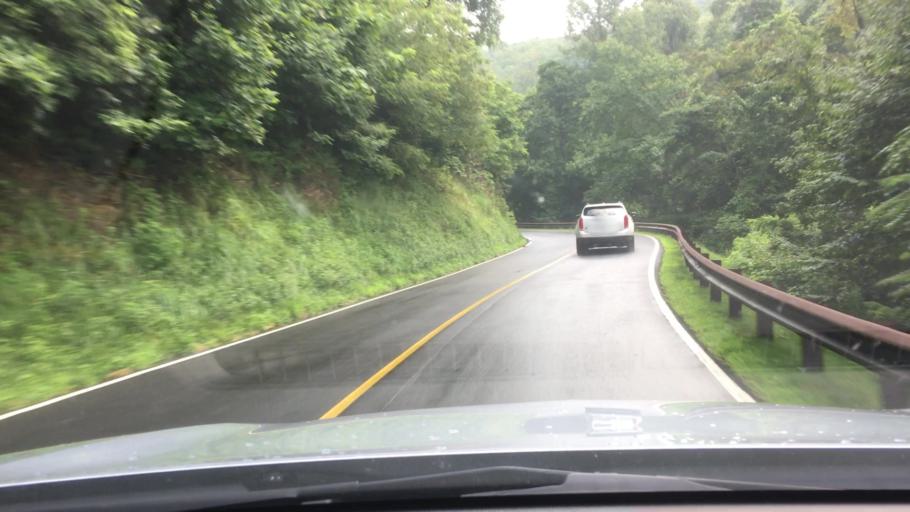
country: US
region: North Carolina
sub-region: Yancey County
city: Burnsville
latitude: 35.8867
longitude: -82.3523
